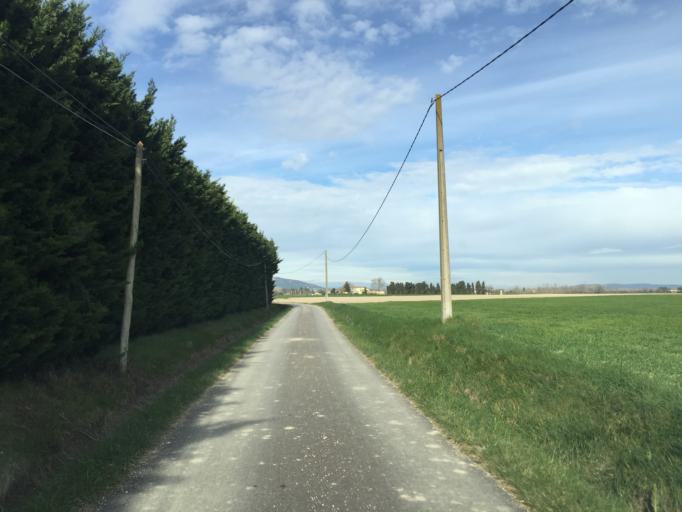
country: FR
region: Provence-Alpes-Cote d'Azur
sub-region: Departement du Vaucluse
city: Caderousse
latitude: 44.1095
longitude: 4.7529
